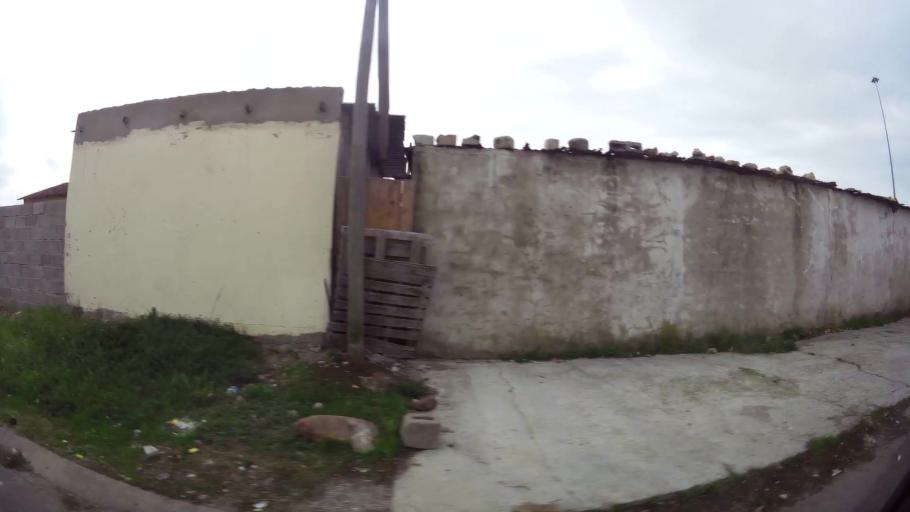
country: ZA
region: Eastern Cape
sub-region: Nelson Mandela Bay Metropolitan Municipality
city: Port Elizabeth
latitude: -33.8941
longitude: 25.6065
